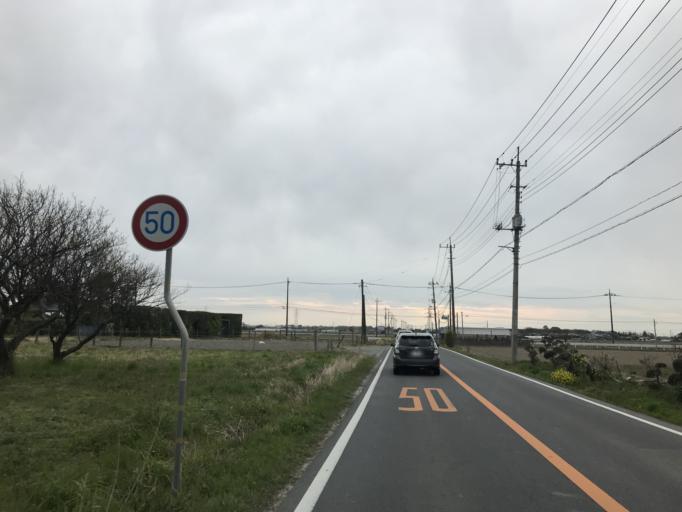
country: JP
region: Ibaraki
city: Mitsukaido
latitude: 35.9890
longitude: 140.0093
